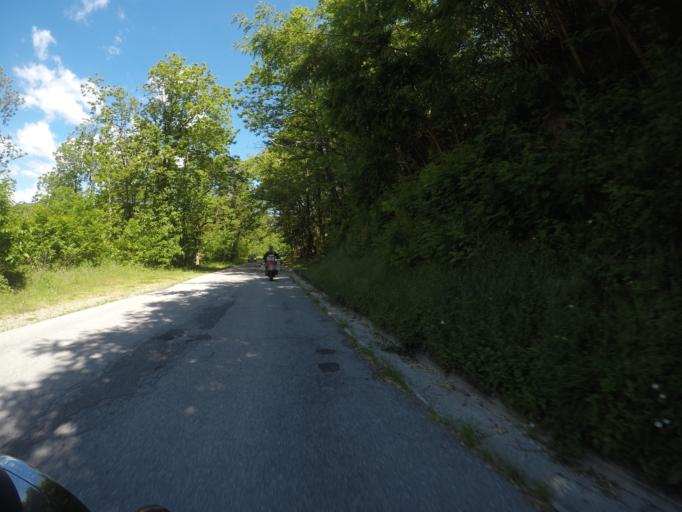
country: IT
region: Tuscany
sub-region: Provincia di Lucca
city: Careggine
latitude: 44.1282
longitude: 10.3360
